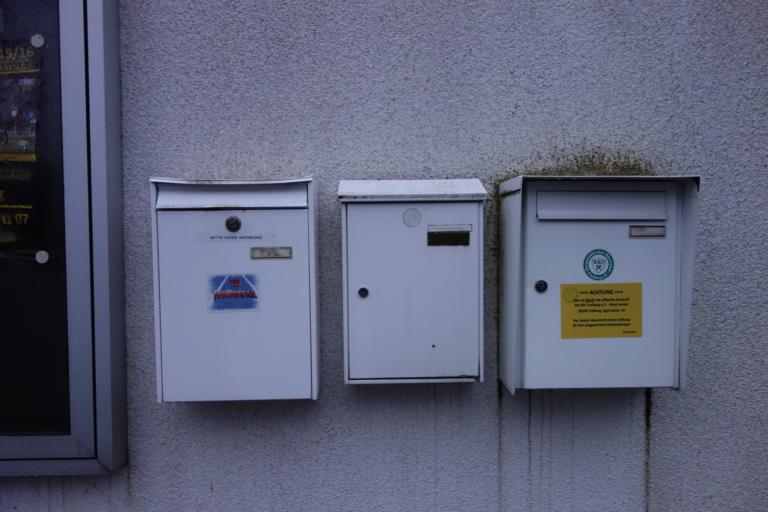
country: DE
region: Saxony
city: Freiberg
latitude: 50.9071
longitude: 13.3158
